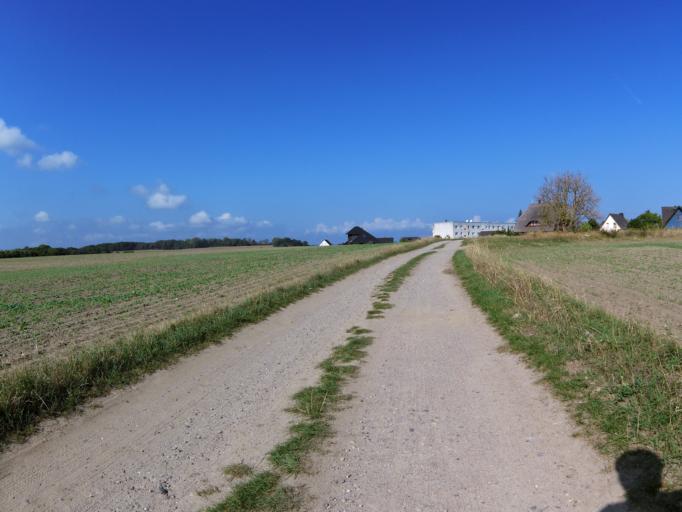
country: DE
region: Mecklenburg-Vorpommern
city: Seebad Bansin
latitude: 53.9662
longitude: 14.0635
